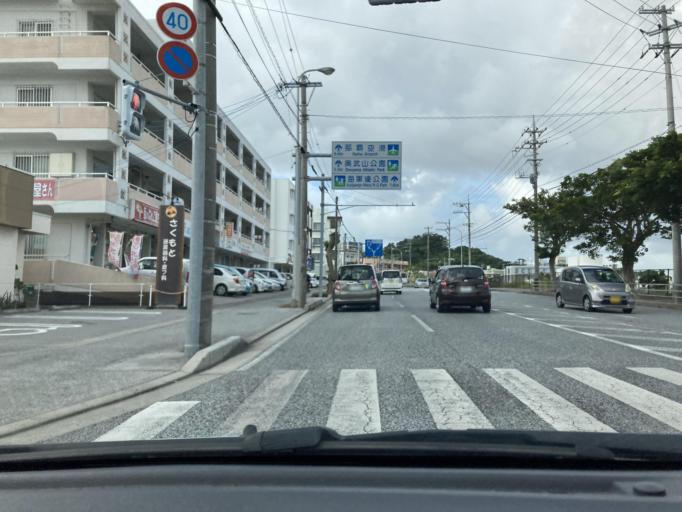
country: JP
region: Okinawa
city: Tomigusuku
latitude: 26.1800
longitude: 127.6811
